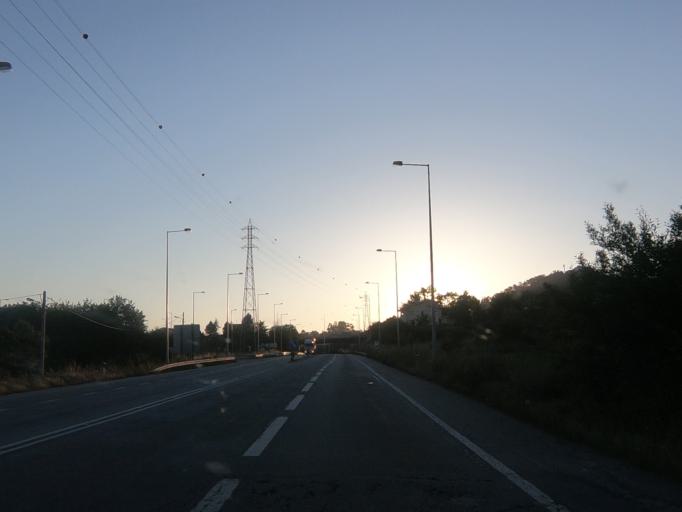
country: PT
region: Viseu
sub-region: Viseu
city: Abraveses
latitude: 40.6918
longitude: -7.9093
